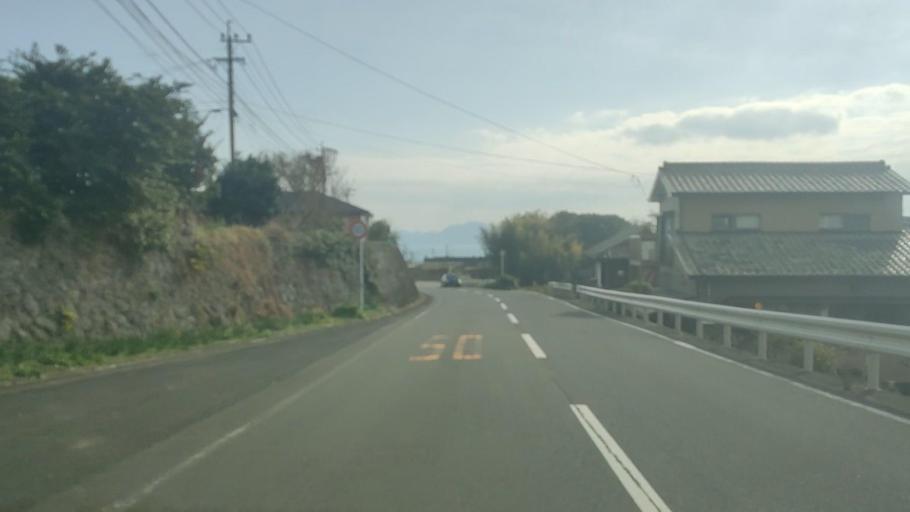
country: JP
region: Nagasaki
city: Shimabara
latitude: 32.6663
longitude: 130.2865
